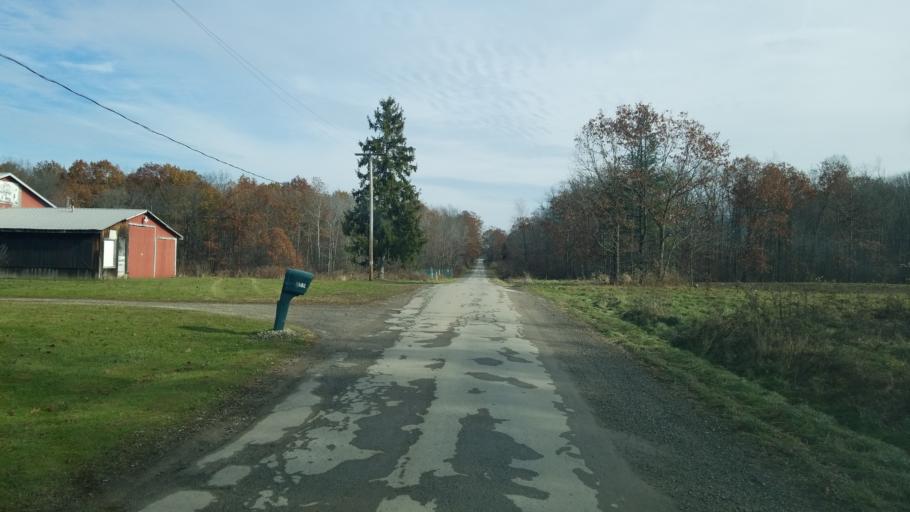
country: US
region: Ohio
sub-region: Ashtabula County
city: Roaming Shores
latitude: 41.6432
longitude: -80.7928
